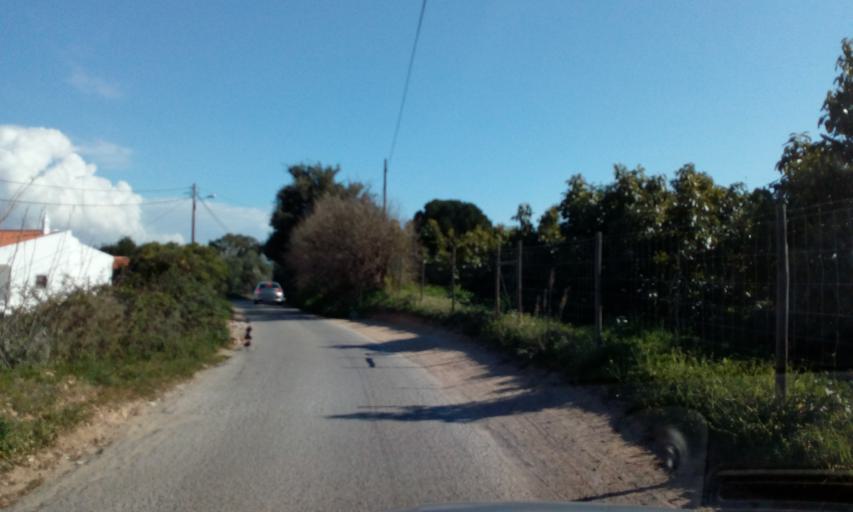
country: PT
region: Faro
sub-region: Albufeira
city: Ferreiras
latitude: 37.1047
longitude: -8.2091
